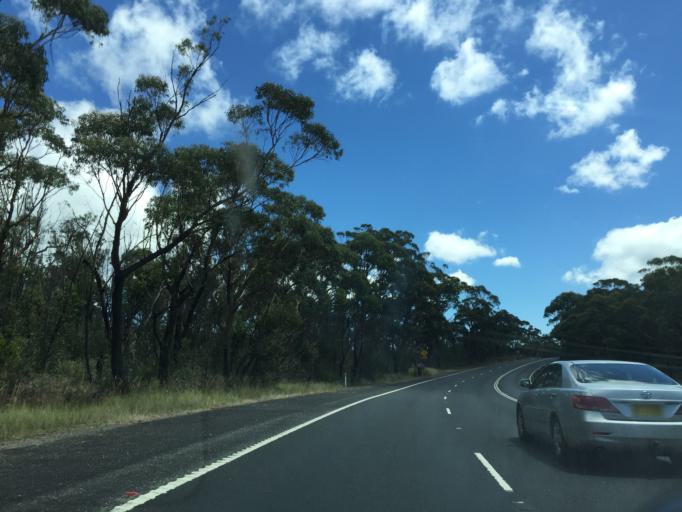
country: AU
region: New South Wales
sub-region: Blue Mountains Municipality
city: Blackheath
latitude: -33.5720
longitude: 150.3582
